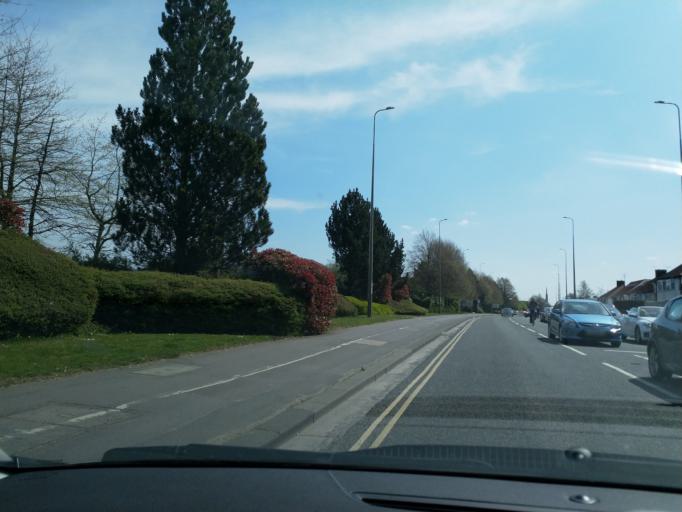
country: GB
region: England
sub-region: Oxfordshire
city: Cowley
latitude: 51.7338
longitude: -1.2098
